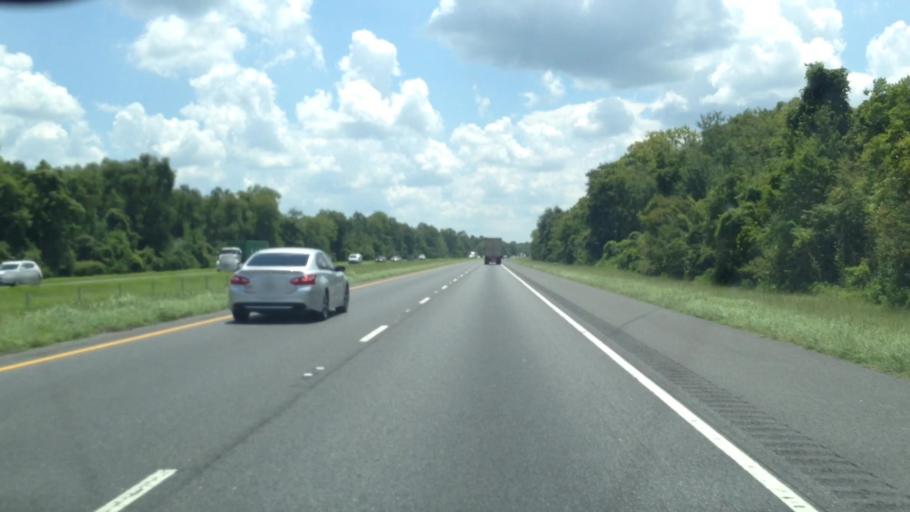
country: US
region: Louisiana
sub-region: Ascension Parish
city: Sorrento
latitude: 30.1500
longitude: -90.7842
